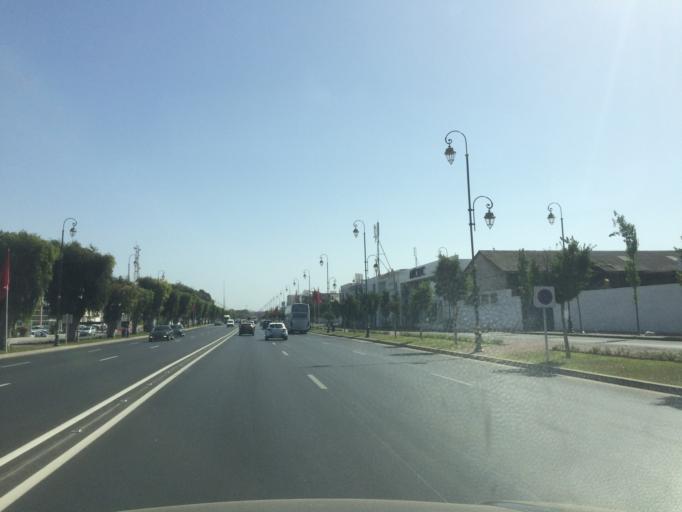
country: MA
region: Rabat-Sale-Zemmour-Zaer
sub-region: Rabat
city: Rabat
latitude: 33.9848
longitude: -6.8707
